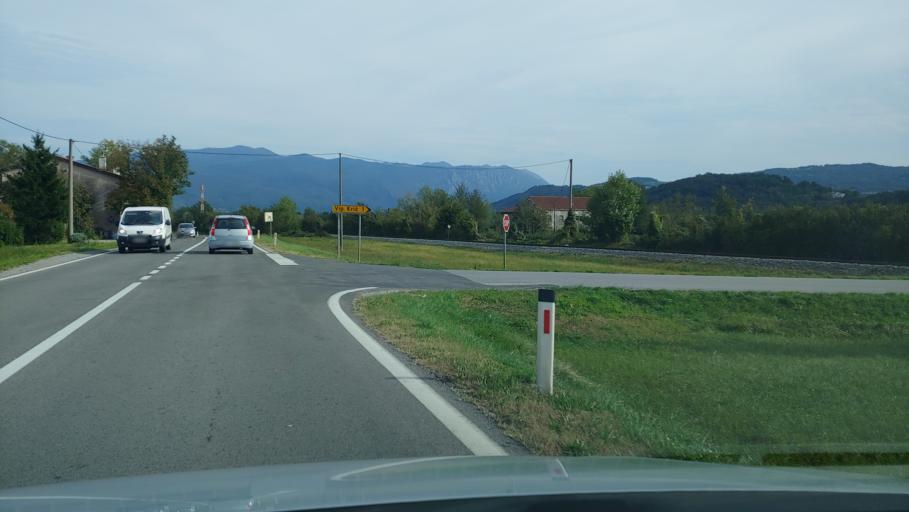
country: SI
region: Ajdovscina
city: Lokavec
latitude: 45.8870
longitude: 13.8681
